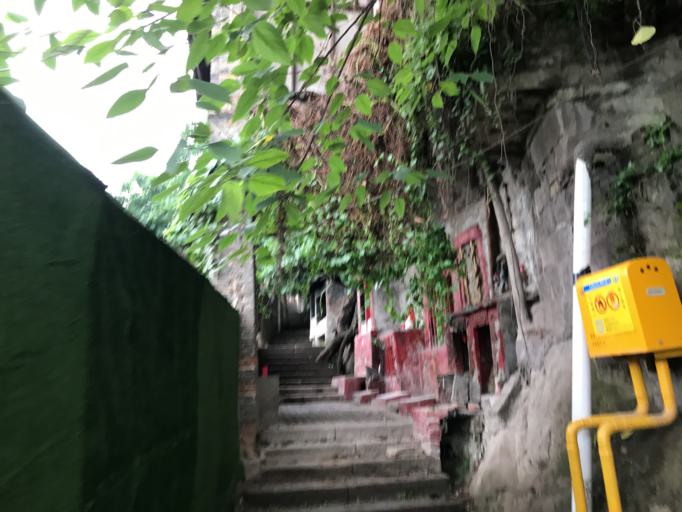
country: CN
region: Chongqing Shi
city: Nanping
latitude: 29.5595
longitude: 106.5908
